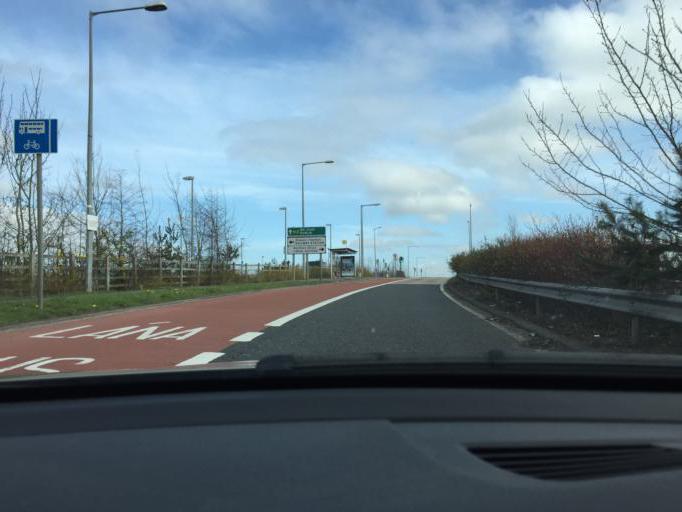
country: IE
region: Leinster
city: Castleknock
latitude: 53.3772
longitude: -6.3466
